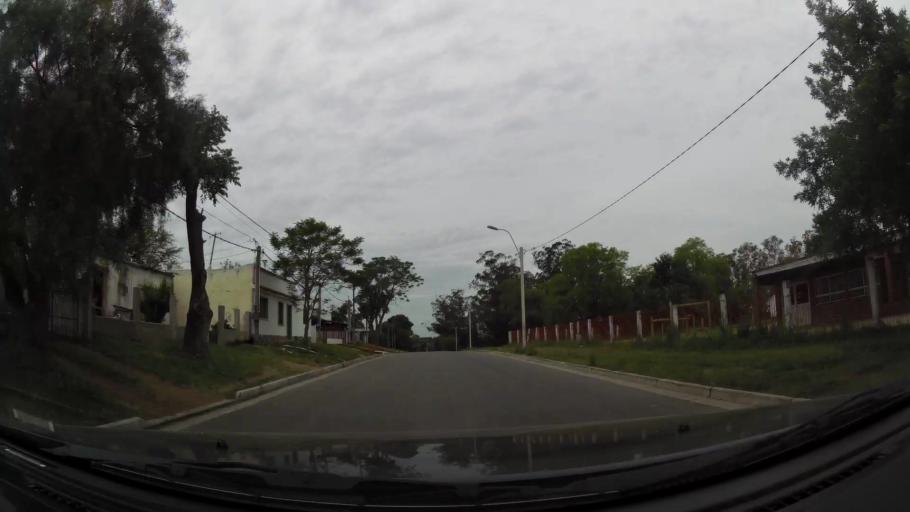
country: UY
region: Canelones
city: Las Piedras
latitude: -34.7242
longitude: -56.2011
